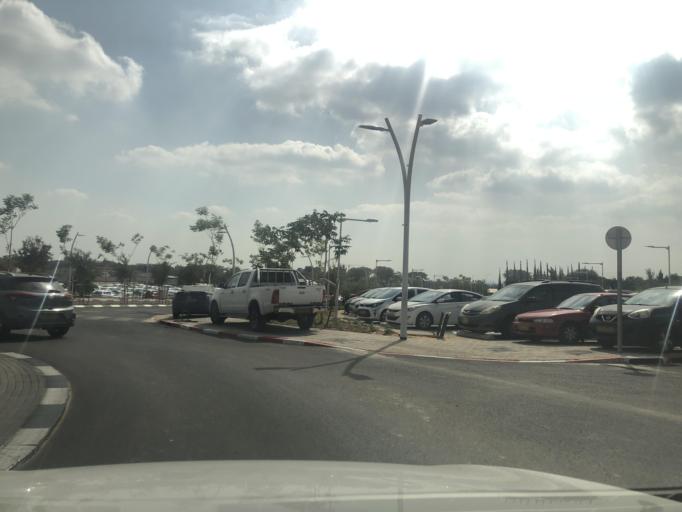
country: IL
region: Tel Aviv
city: Or Yehuda
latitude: 32.0440
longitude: 34.8426
